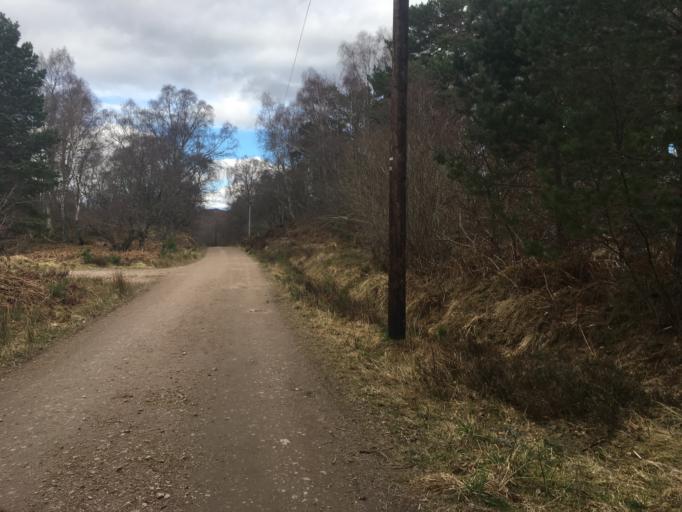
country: GB
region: Scotland
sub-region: Highland
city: Aviemore
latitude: 57.1634
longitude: -3.8136
